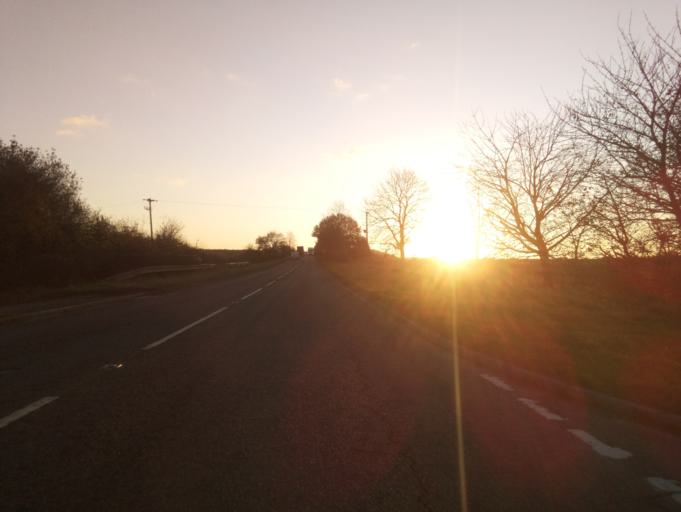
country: GB
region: England
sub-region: Wiltshire
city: Upton Scudamore
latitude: 51.2236
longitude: -2.1920
